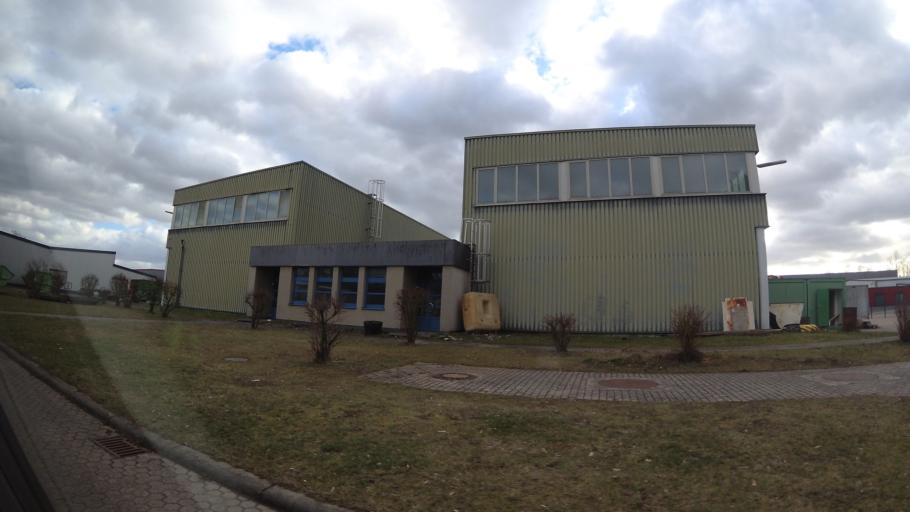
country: DE
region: Saarland
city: Bexbach
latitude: 49.3616
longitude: 7.2727
